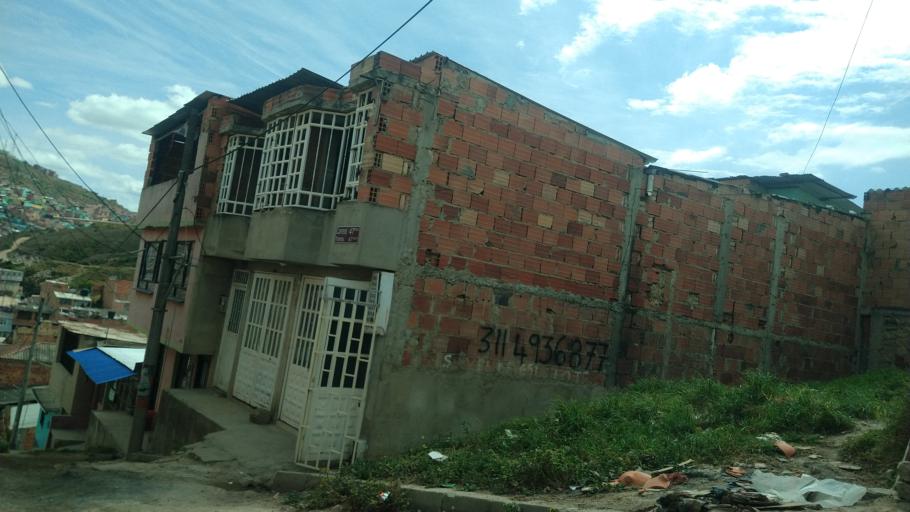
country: CO
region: Cundinamarca
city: Soacha
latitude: 4.5681
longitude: -74.1814
